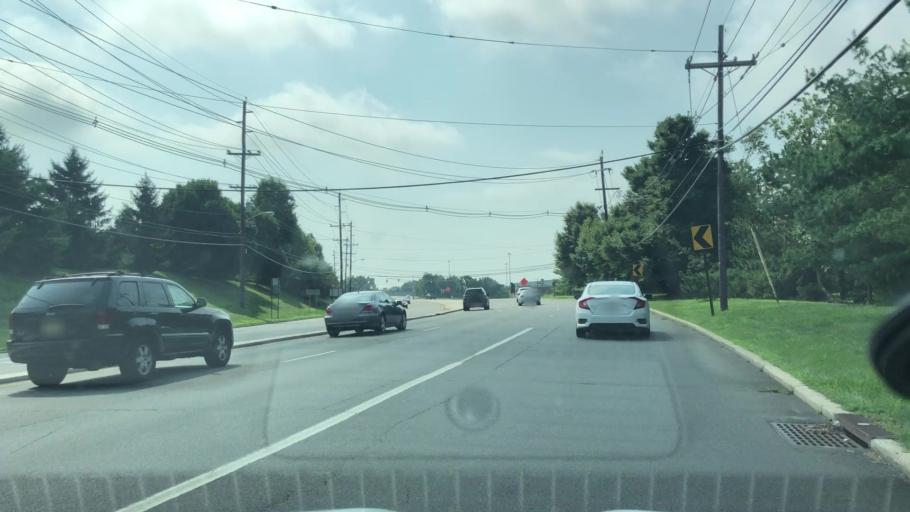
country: US
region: New Jersey
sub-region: Mercer County
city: Lawrenceville
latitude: 40.3014
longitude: -74.6829
